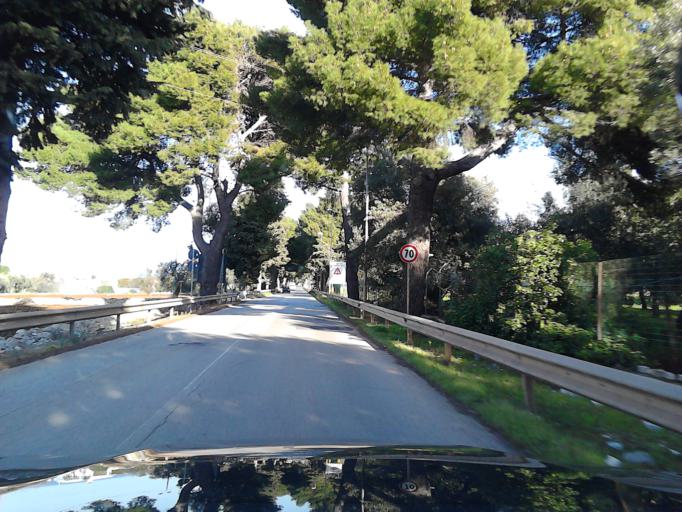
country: IT
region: Apulia
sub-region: Provincia di Bari
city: Mola di Bari
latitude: 41.0400
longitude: 17.0565
